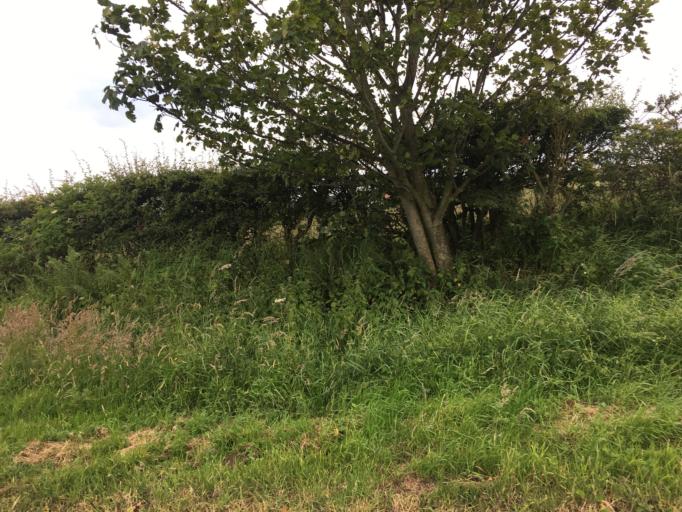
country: GB
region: England
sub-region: Northumberland
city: Lowick
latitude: 55.6556
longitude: -1.9021
